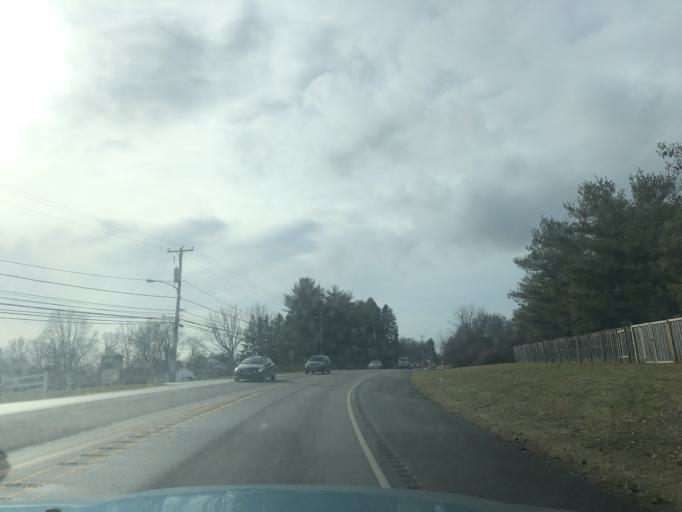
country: US
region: Pennsylvania
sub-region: Montgomery County
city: Harleysville
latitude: 40.2724
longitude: -75.3958
